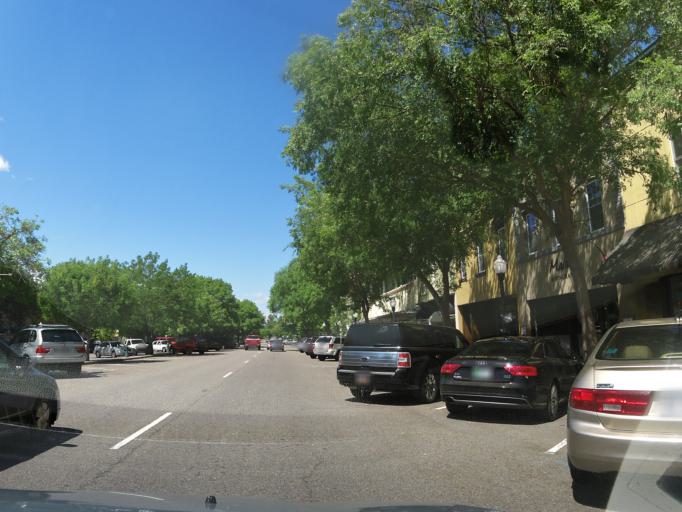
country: US
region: South Carolina
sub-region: Aiken County
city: Aiken
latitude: 33.5607
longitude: -81.7228
